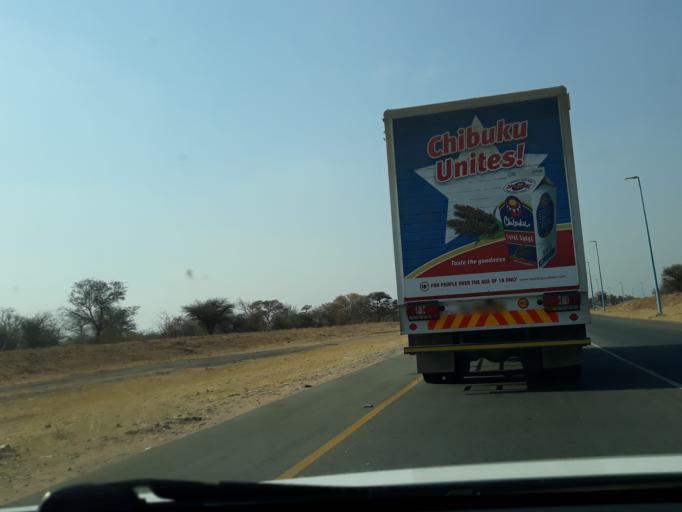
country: BW
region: Central
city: Tonota
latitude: -21.4262
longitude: 27.4412
